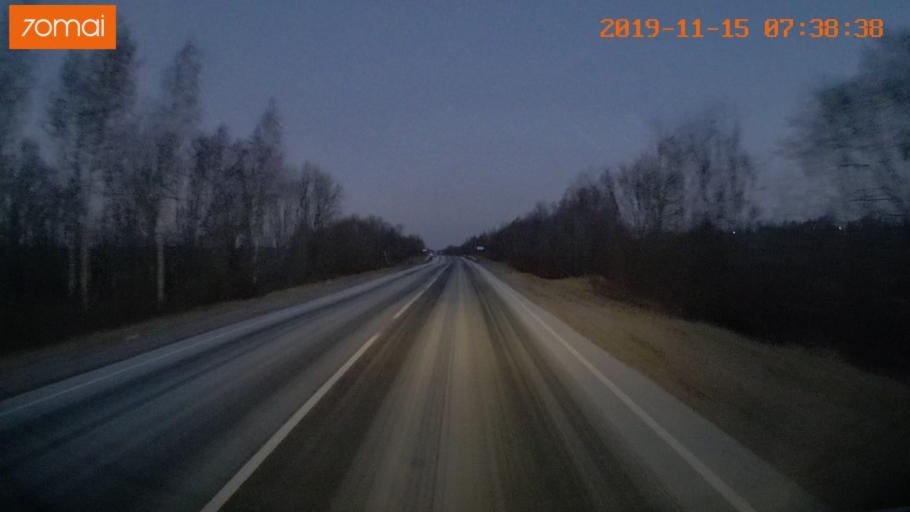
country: RU
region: Vologda
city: Sheksna
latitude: 58.7590
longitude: 38.3975
